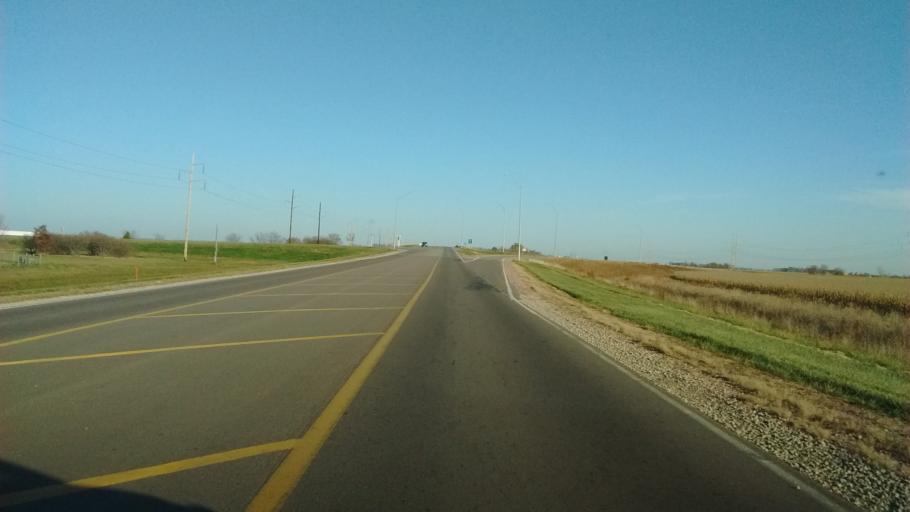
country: US
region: Iowa
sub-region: Woodbury County
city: Sergeant Bluff
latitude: 42.3299
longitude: -96.3238
